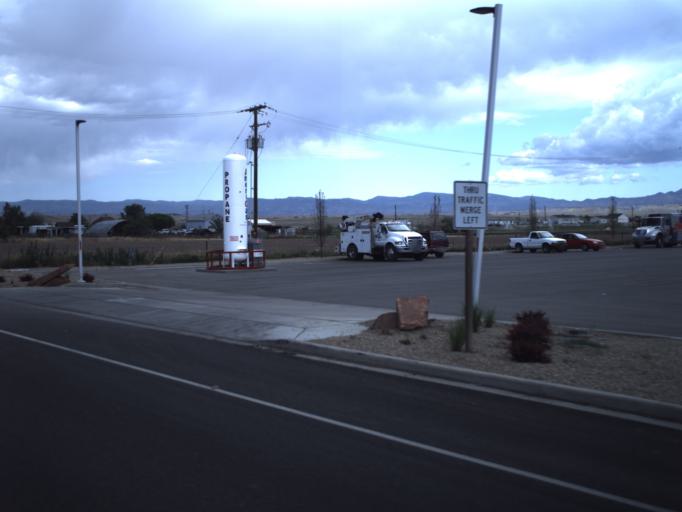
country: US
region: Utah
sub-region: Carbon County
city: Wellington
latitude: 39.5426
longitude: -110.6895
